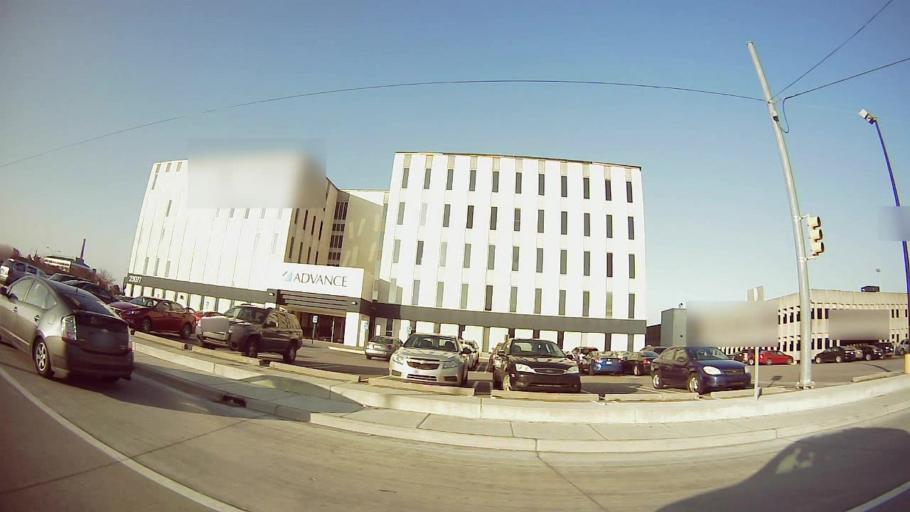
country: US
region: Michigan
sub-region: Oakland County
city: Oak Park
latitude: 42.4599
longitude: -83.2013
